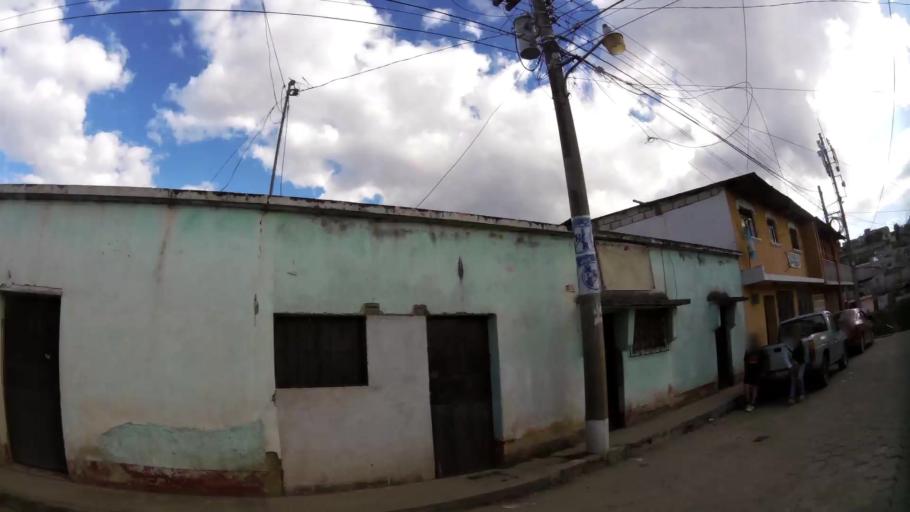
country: GT
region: Quetzaltenango
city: Quetzaltenango
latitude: 14.8513
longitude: -91.5169
